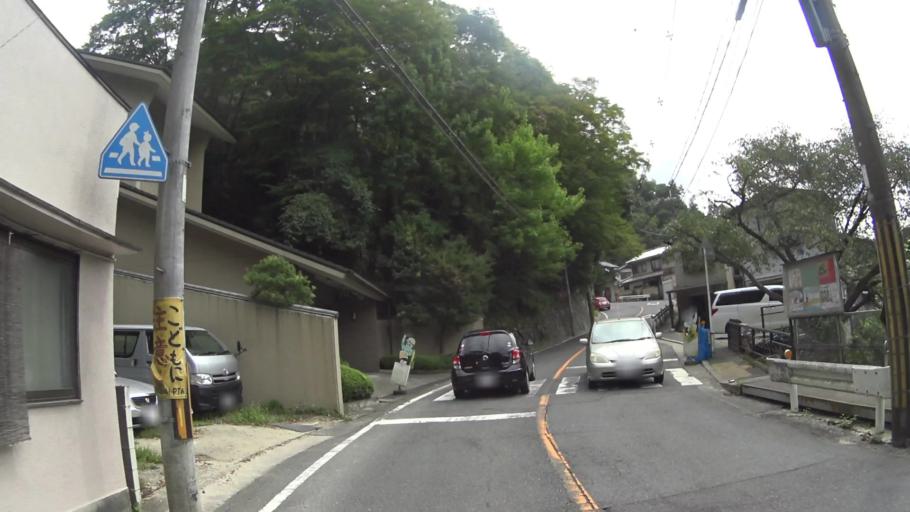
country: JP
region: Kyoto
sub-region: Kyoto-shi
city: Kamigyo-ku
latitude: 35.0320
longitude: 135.7996
